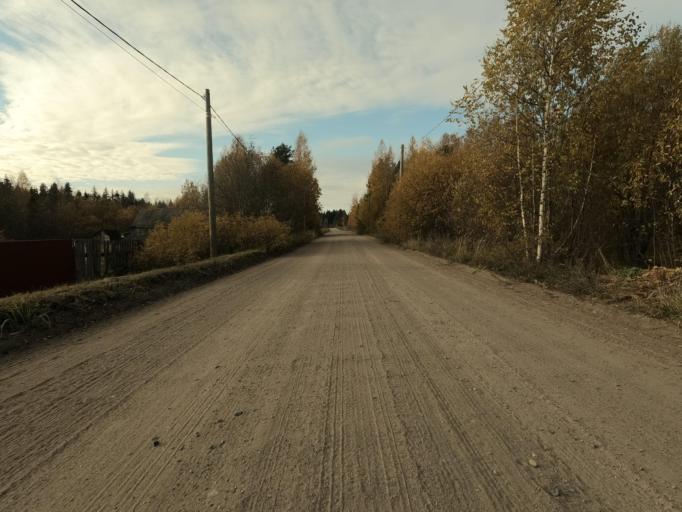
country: RU
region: Leningrad
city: Priladozhskiy
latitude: 59.6294
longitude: 31.4038
